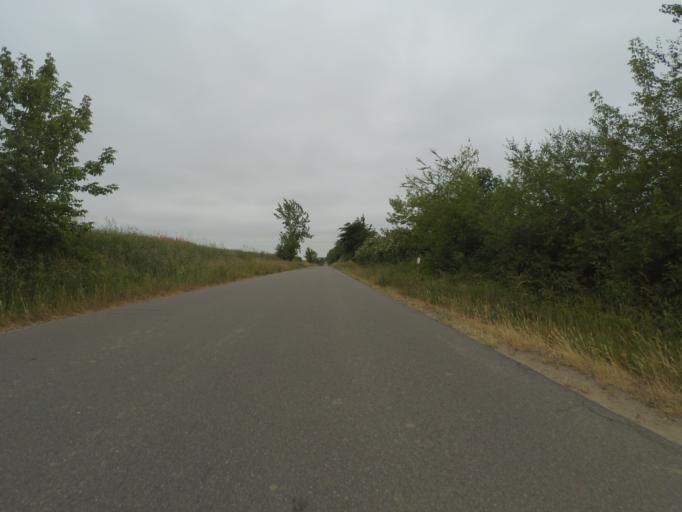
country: DE
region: Mecklenburg-Vorpommern
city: Goldberg
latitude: 53.5641
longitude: 12.1071
